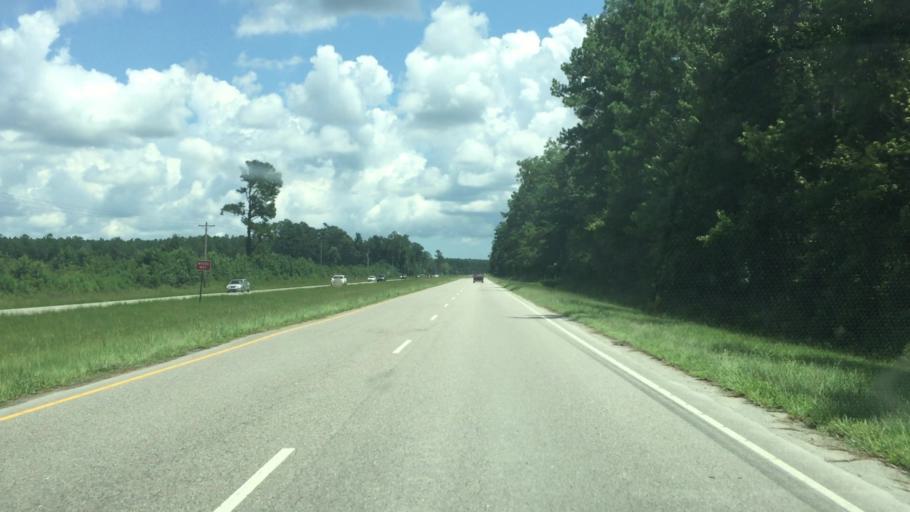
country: US
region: South Carolina
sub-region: Horry County
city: Loris
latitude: 34.0117
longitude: -78.7765
